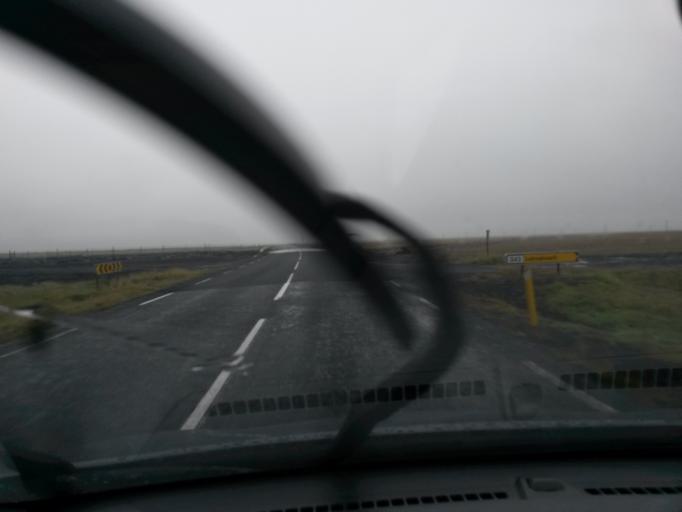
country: IS
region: South
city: Vestmannaeyjar
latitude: 63.5360
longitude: -19.6404
